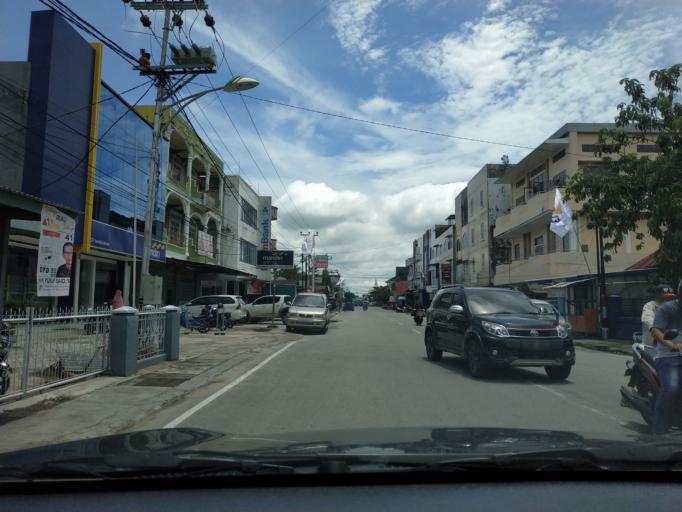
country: ID
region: Riau
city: Tembilahan
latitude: -0.3238
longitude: 103.1587
